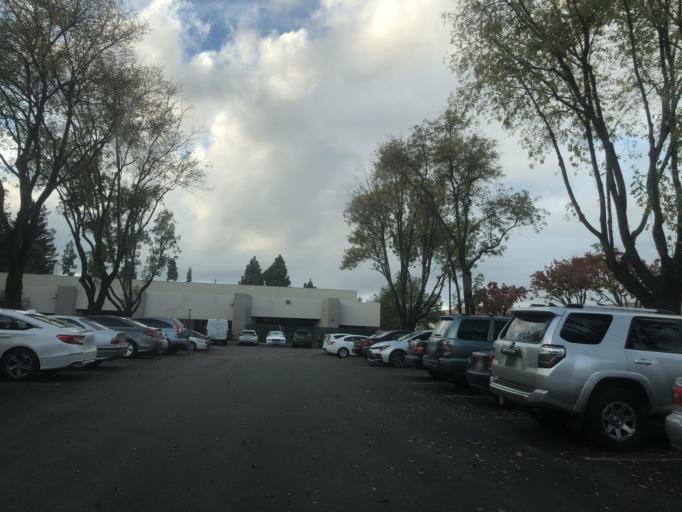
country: US
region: California
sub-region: Santa Clara County
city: San Jose
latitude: 37.3771
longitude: -121.9163
